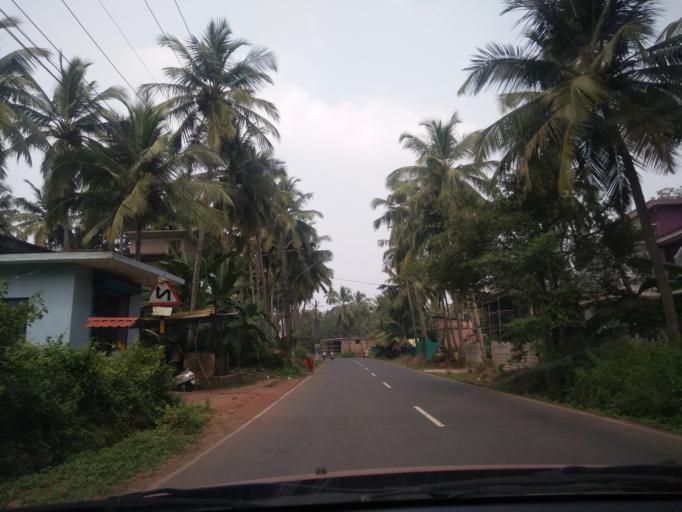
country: IN
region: Goa
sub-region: North Goa
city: Goa Velha
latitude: 15.4356
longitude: 73.8948
